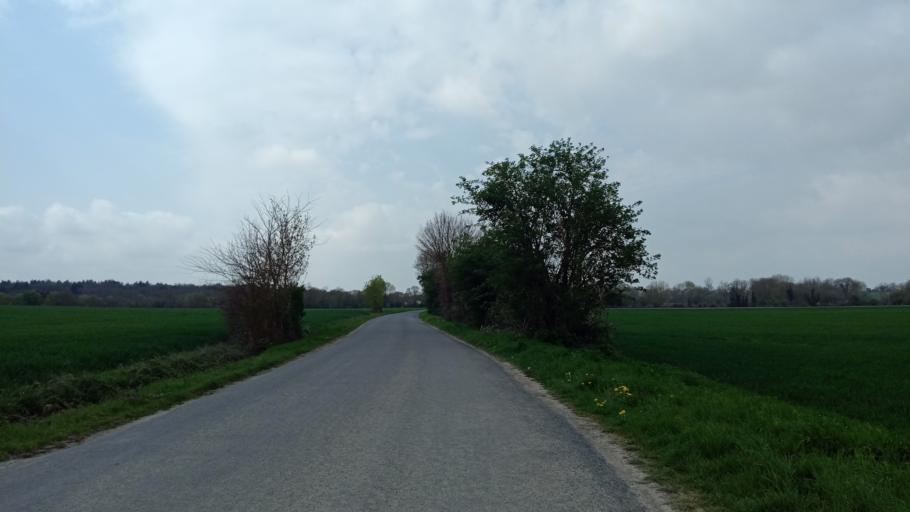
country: FR
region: Poitou-Charentes
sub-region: Departement de la Charente-Maritime
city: Verines
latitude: 46.1513
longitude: -0.9331
